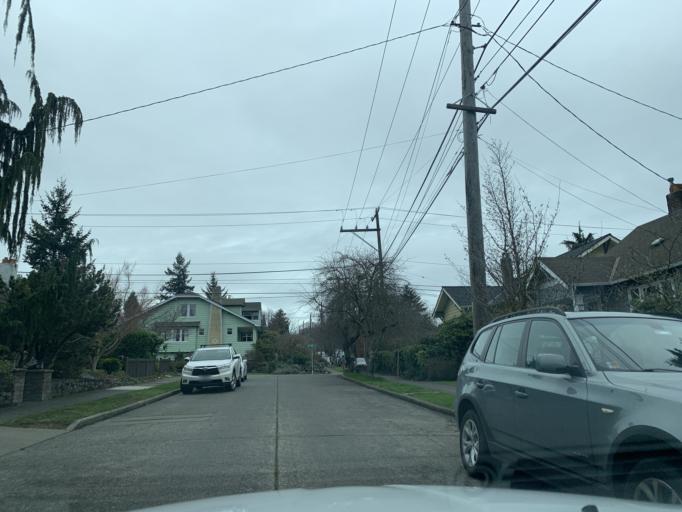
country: US
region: Washington
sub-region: King County
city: Seattle
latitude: 47.6645
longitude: -122.2892
